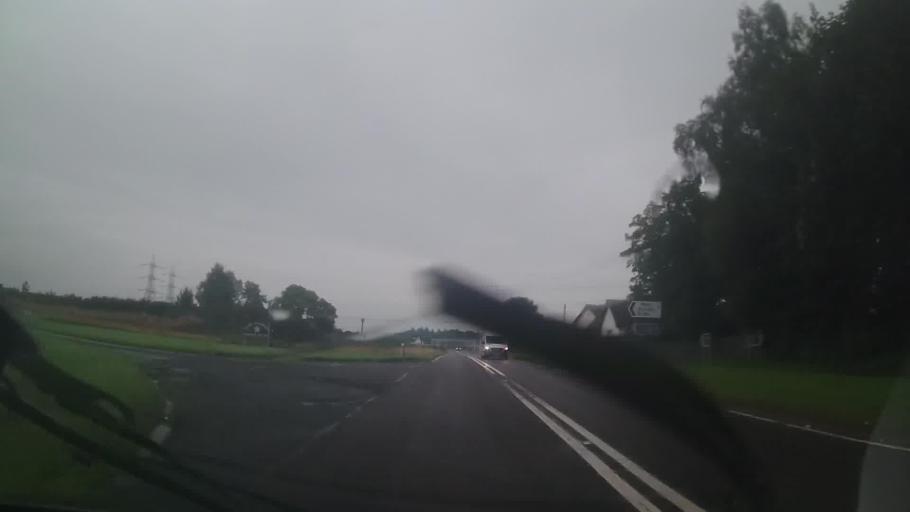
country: GB
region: Scotland
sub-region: North Ayrshire
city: West Kilbride
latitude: 55.7095
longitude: -4.8680
